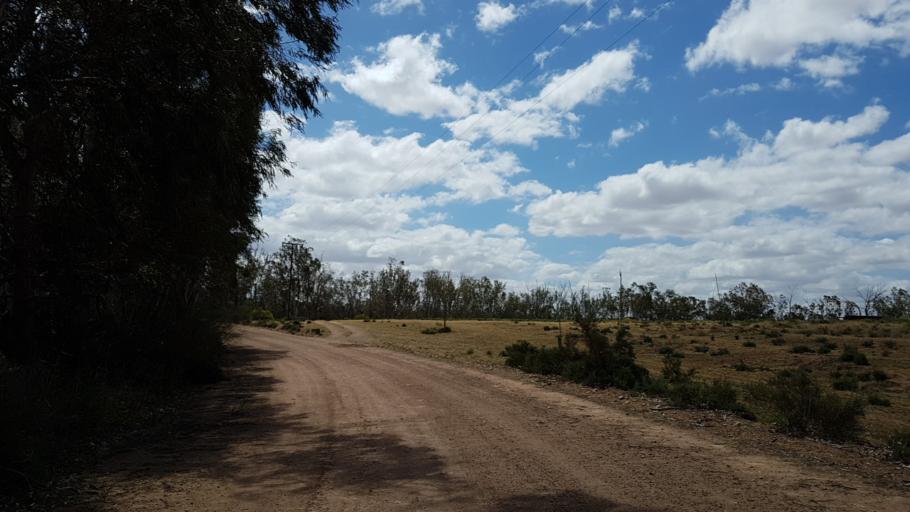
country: AU
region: South Australia
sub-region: Loxton Waikerie
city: Waikerie
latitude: -34.1663
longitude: 140.0252
